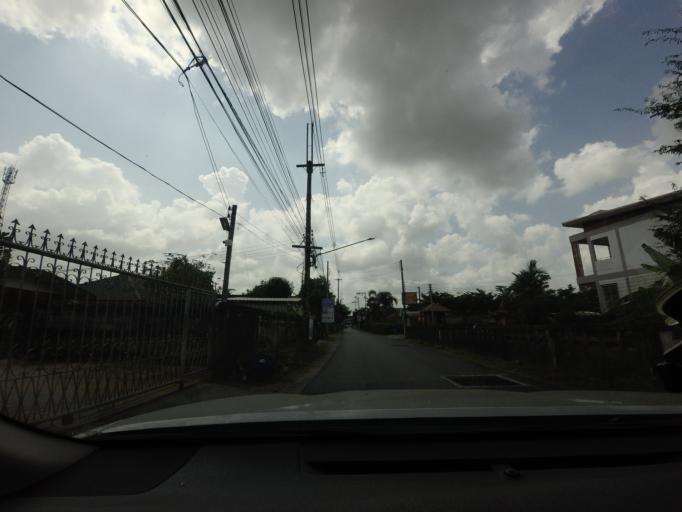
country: TH
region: Nakhon Si Thammarat
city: Nakhon Si Thammarat
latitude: 8.4359
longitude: 99.9310
